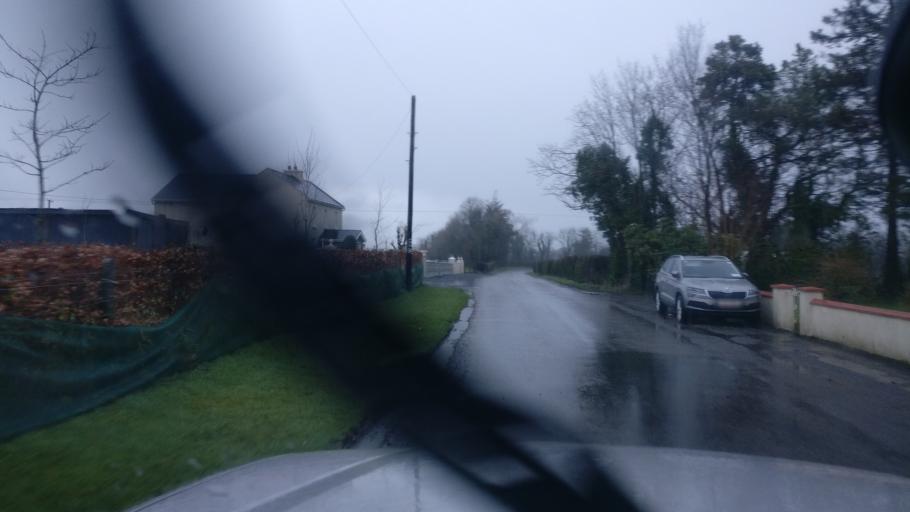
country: IE
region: Connaught
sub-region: County Galway
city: Ballinasloe
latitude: 53.3106
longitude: -8.3599
